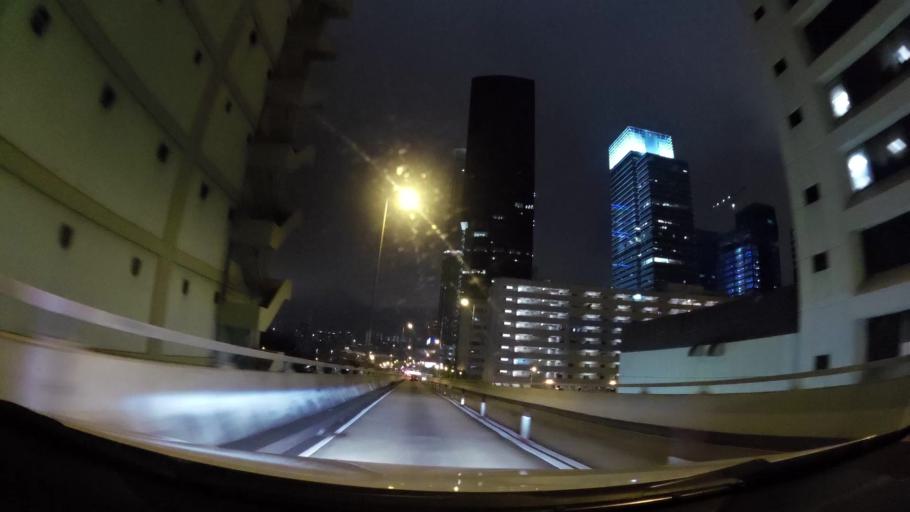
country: HK
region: Kowloon City
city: Kowloon
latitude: 22.3195
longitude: 114.2126
